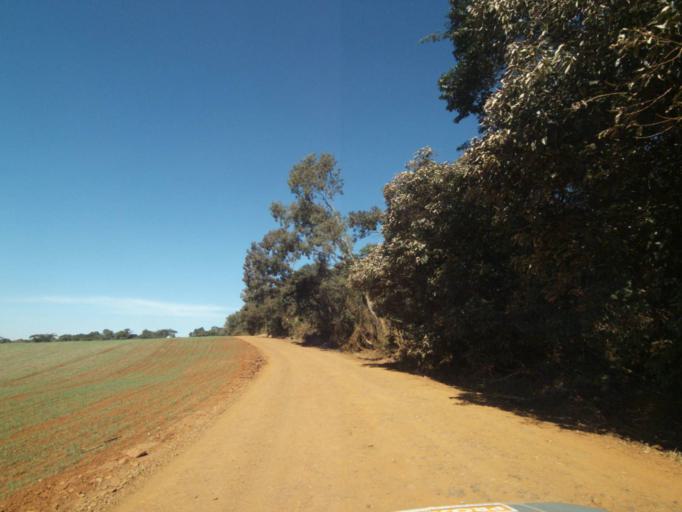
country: BR
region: Parana
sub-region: Tibagi
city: Tibagi
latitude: -24.5725
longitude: -50.6245
